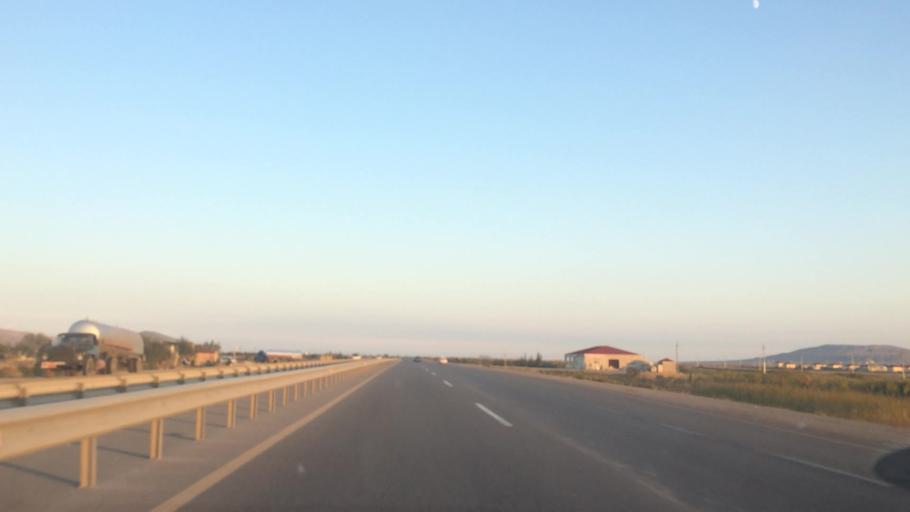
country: AZ
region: Baki
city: Qobustan
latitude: 39.9858
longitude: 49.2090
